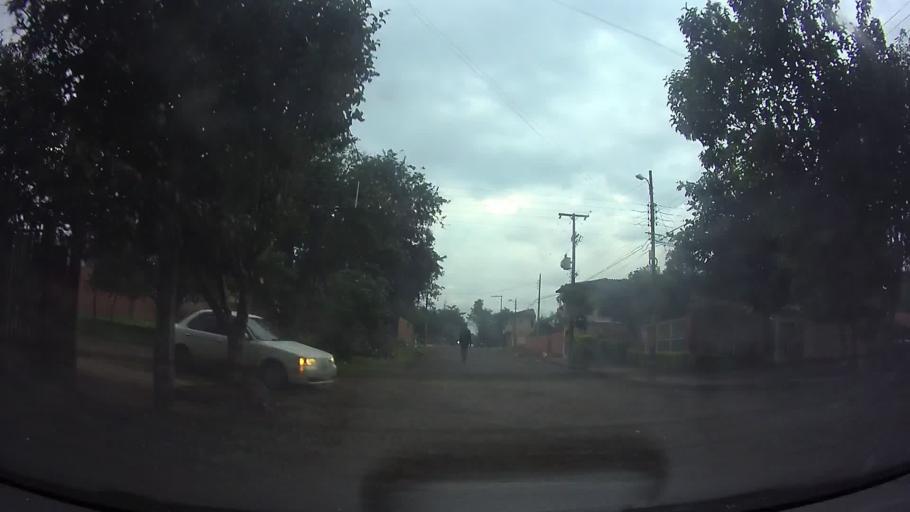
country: PY
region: Central
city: San Lorenzo
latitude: -25.2597
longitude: -57.4921
